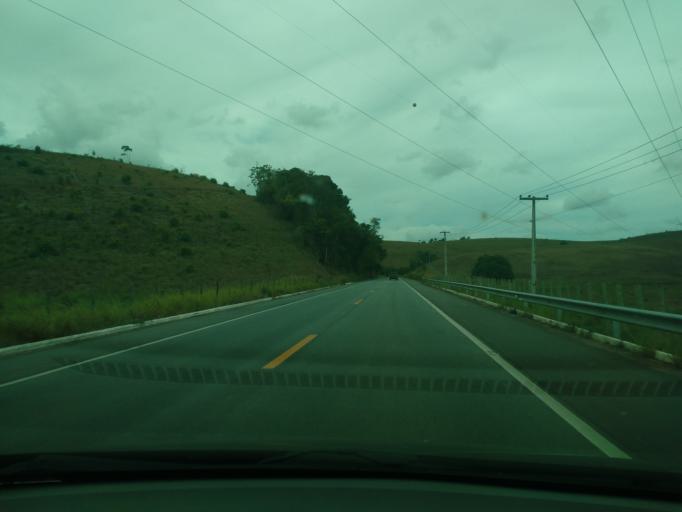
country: BR
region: Alagoas
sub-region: Murici
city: Murici
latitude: -9.2615
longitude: -35.9705
